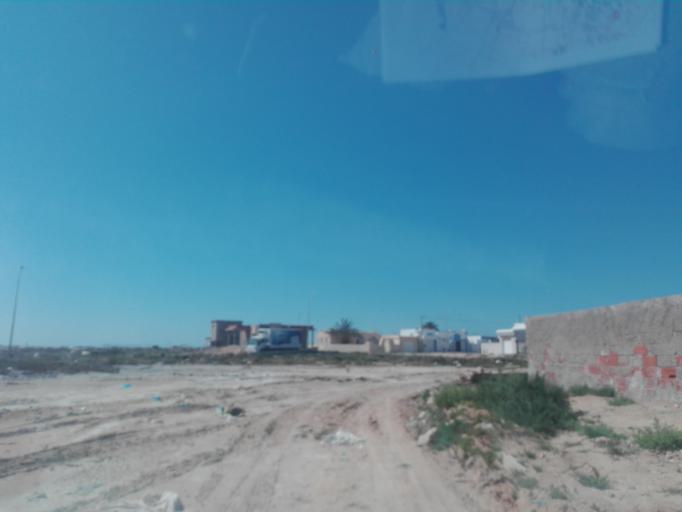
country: TN
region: Safaqis
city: Al Qarmadah
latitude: 34.7028
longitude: 11.1983
